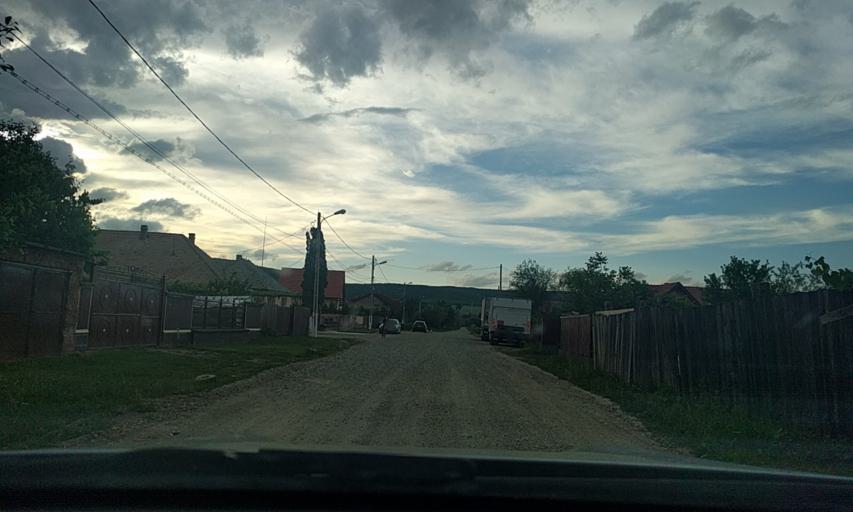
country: RO
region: Covasna
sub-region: Comuna Ilieni
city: Ilieni
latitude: 45.7615
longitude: 25.7224
